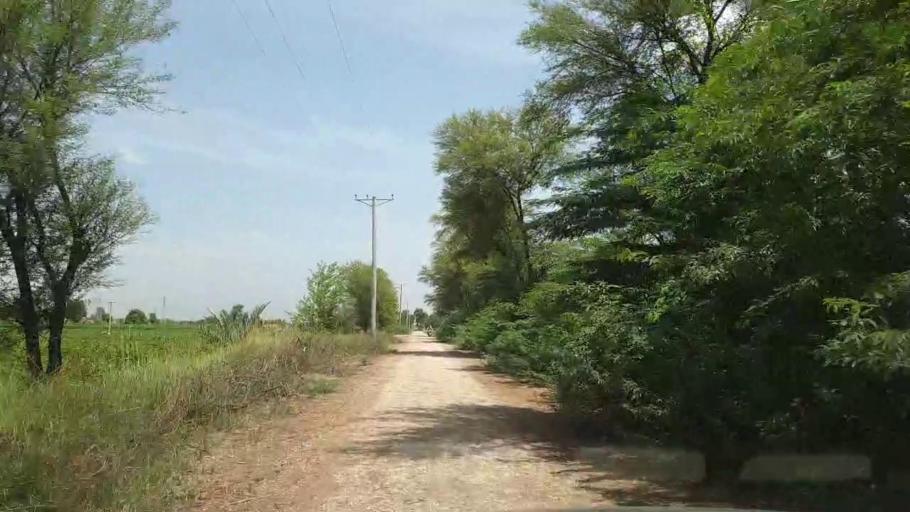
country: PK
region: Sindh
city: Kot Diji
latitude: 27.1487
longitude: 69.0167
